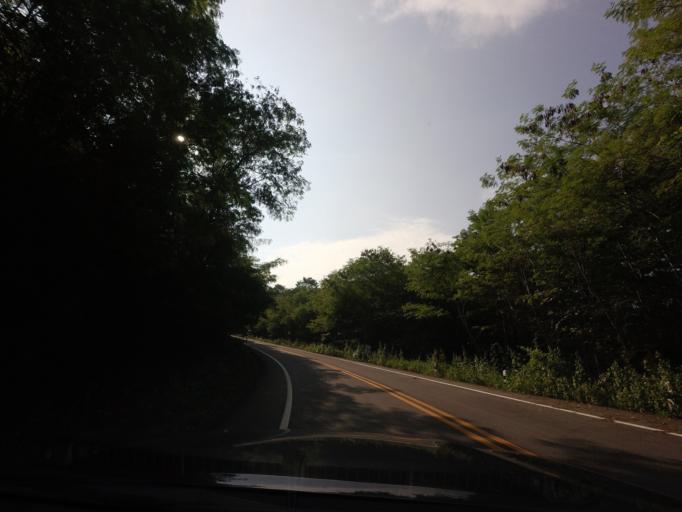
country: TH
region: Nan
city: Na Noi
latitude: 18.3641
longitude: 100.8741
